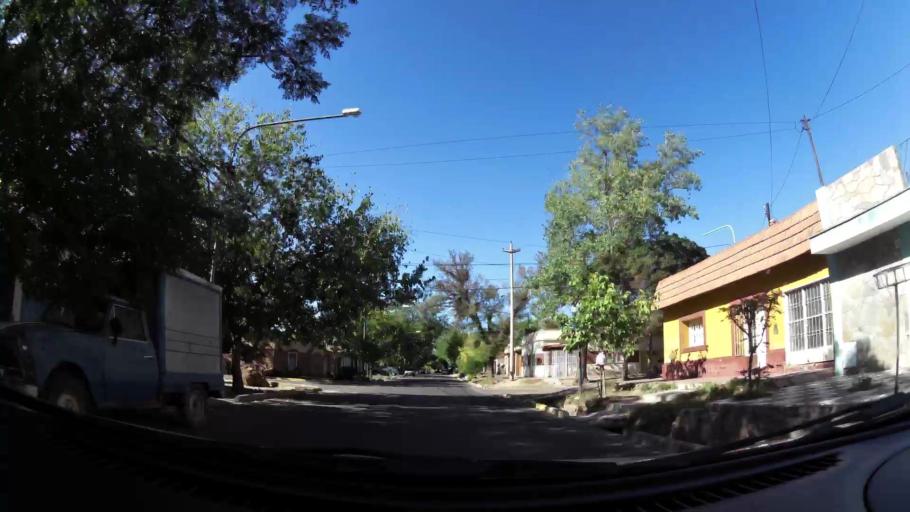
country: AR
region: Mendoza
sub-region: Departamento de Godoy Cruz
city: Godoy Cruz
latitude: -32.9267
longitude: -68.8630
